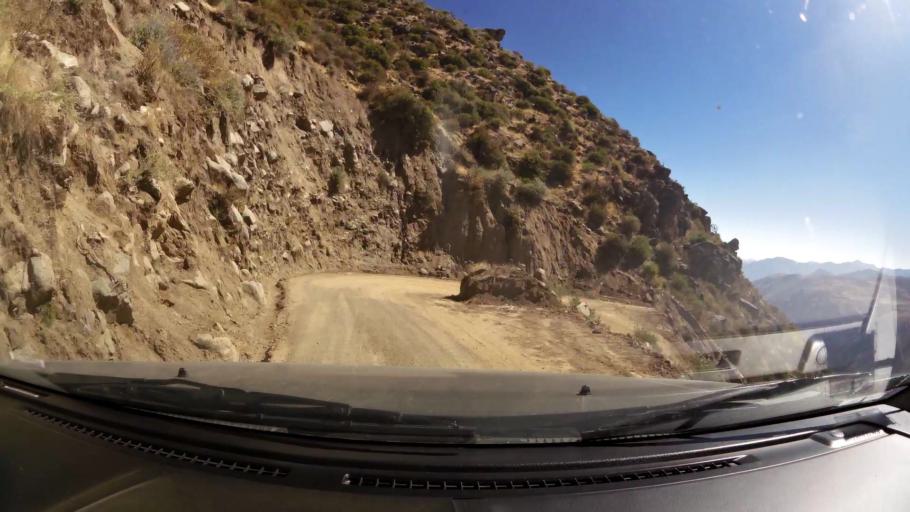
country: PE
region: Huancavelica
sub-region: Huaytara
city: Quito-Arma
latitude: -13.6235
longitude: -75.3550
